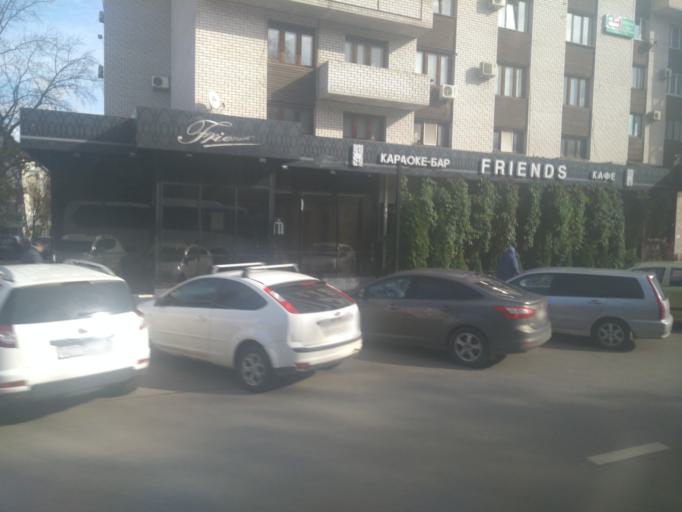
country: RU
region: Tatarstan
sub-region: Gorod Kazan'
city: Kazan
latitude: 55.7991
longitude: 49.1909
